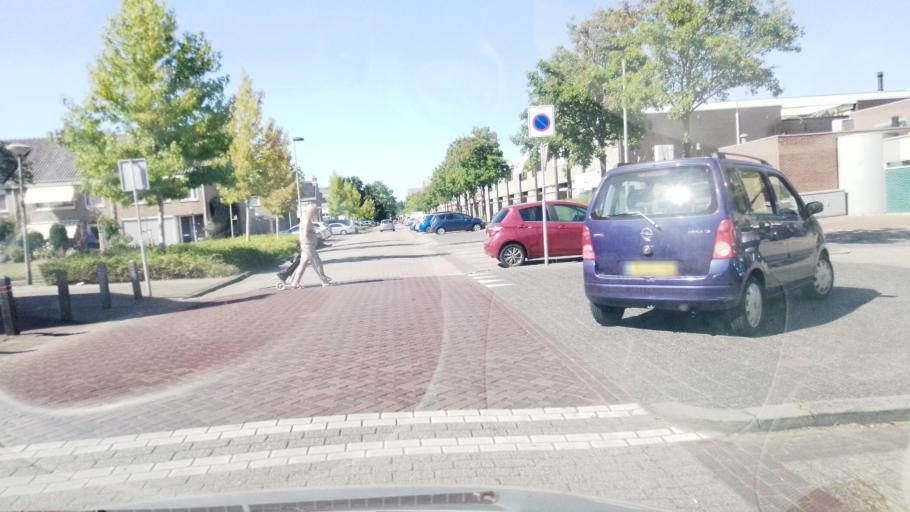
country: NL
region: South Holland
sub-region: Gemeente Vlaardingen
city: Vlaardingen
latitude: 51.9294
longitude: 4.3470
